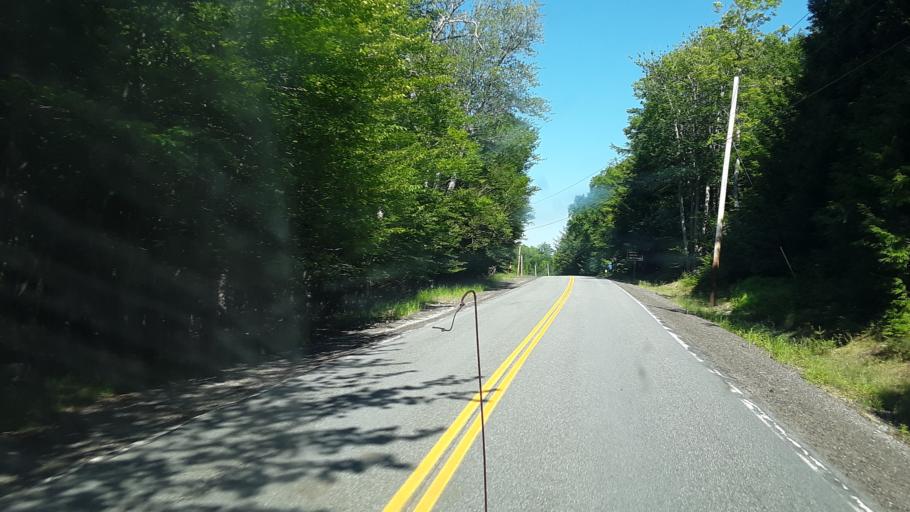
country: US
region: Maine
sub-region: Hancock County
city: Franklin
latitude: 44.6247
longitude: -68.0921
